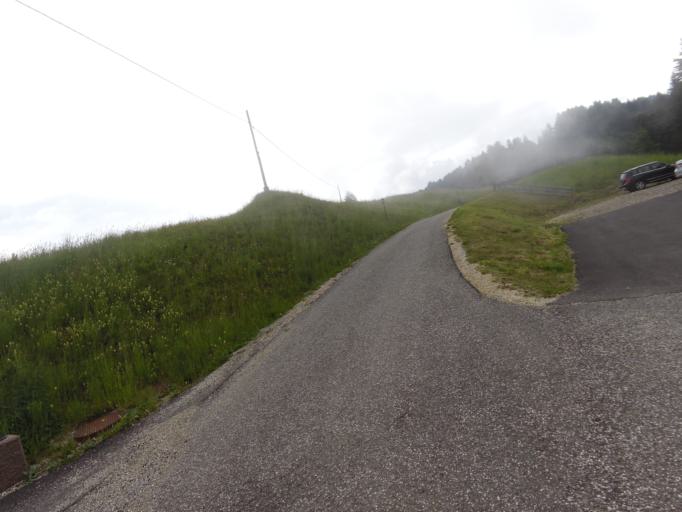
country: IT
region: Trentino-Alto Adige
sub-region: Bolzano
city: Siusi
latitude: 46.5388
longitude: 11.6101
